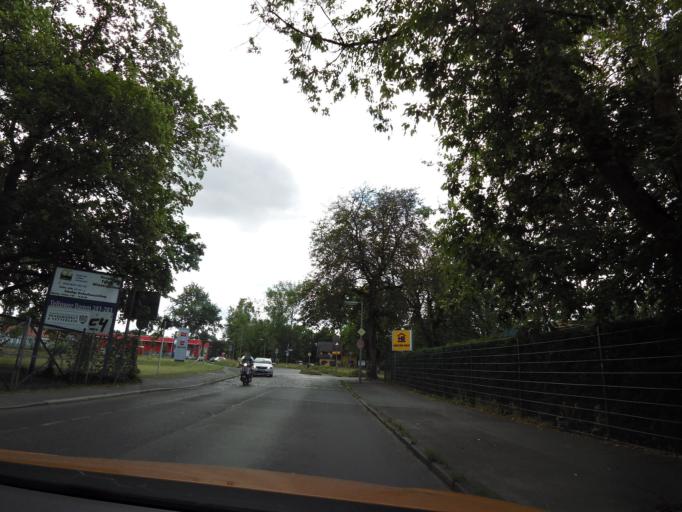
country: DE
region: Brandenburg
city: Teltow
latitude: 52.4075
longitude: 13.2676
